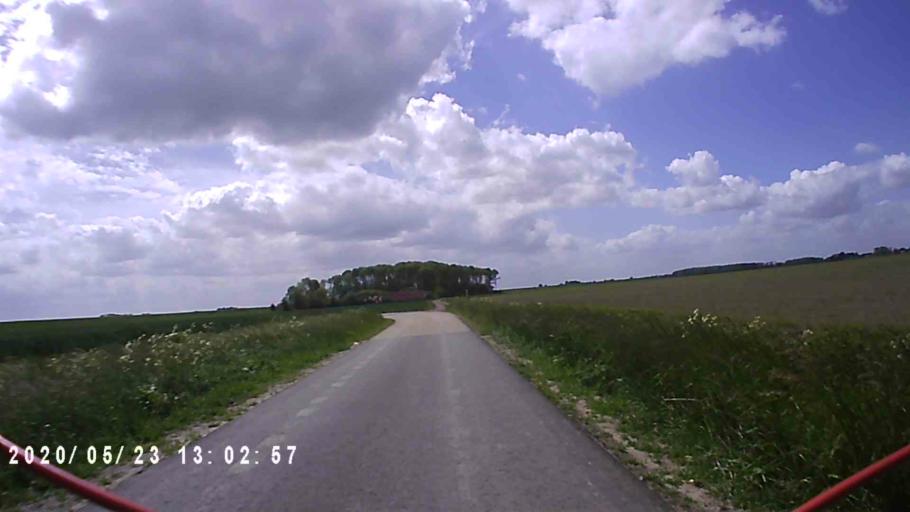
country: NL
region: Groningen
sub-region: Gemeente  Oldambt
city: Winschoten
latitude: 53.2887
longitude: 7.0685
